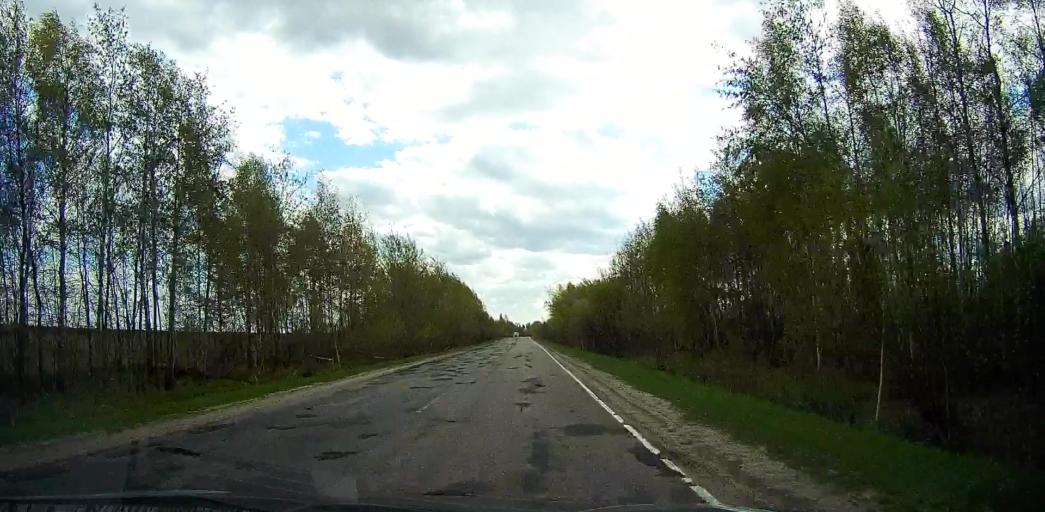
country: RU
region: Moskovskaya
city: Davydovo
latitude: 55.6366
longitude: 38.7472
